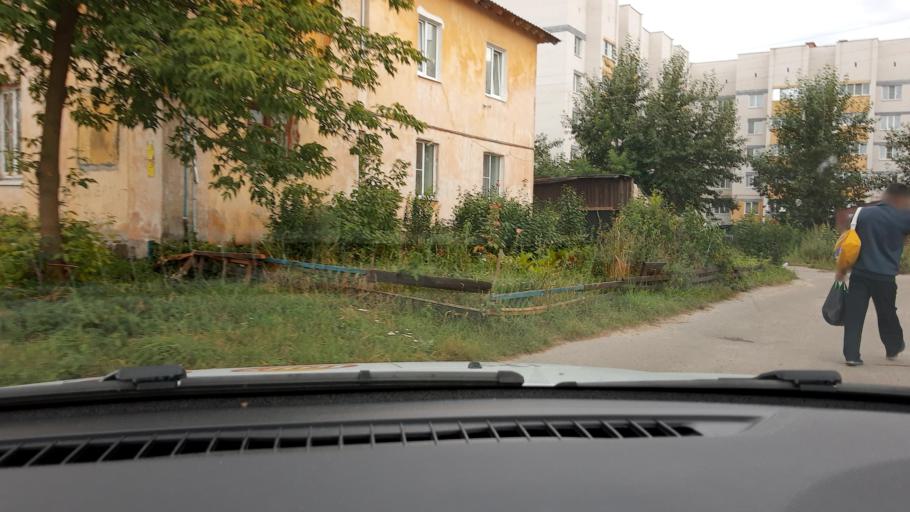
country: RU
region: Nizjnij Novgorod
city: Dzerzhinsk
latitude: 56.2372
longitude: 43.4832
